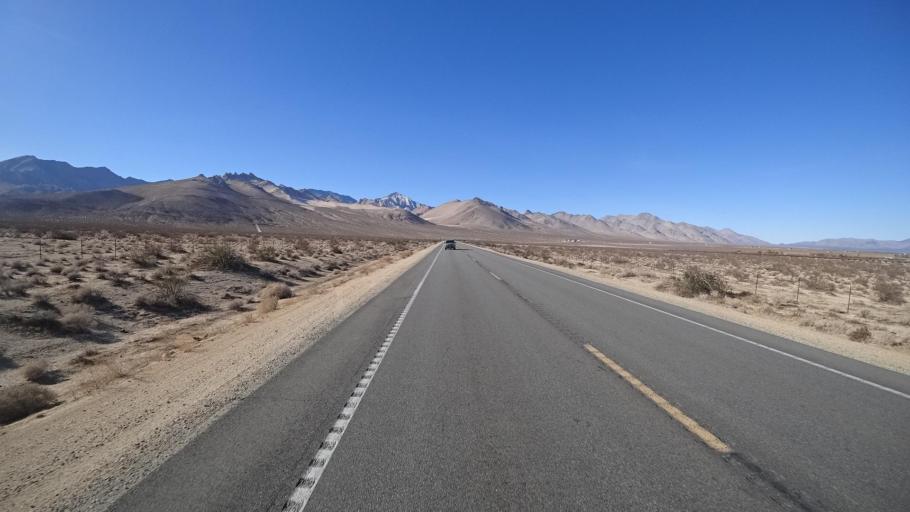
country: US
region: California
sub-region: Kern County
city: Inyokern
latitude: 35.6876
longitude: -117.8543
